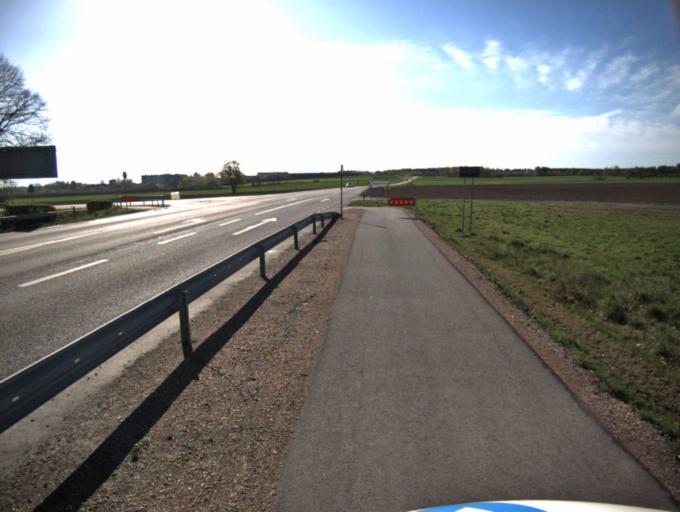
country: SE
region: Skane
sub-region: Kristianstads Kommun
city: Norra Asum
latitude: 55.9999
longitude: 14.1060
